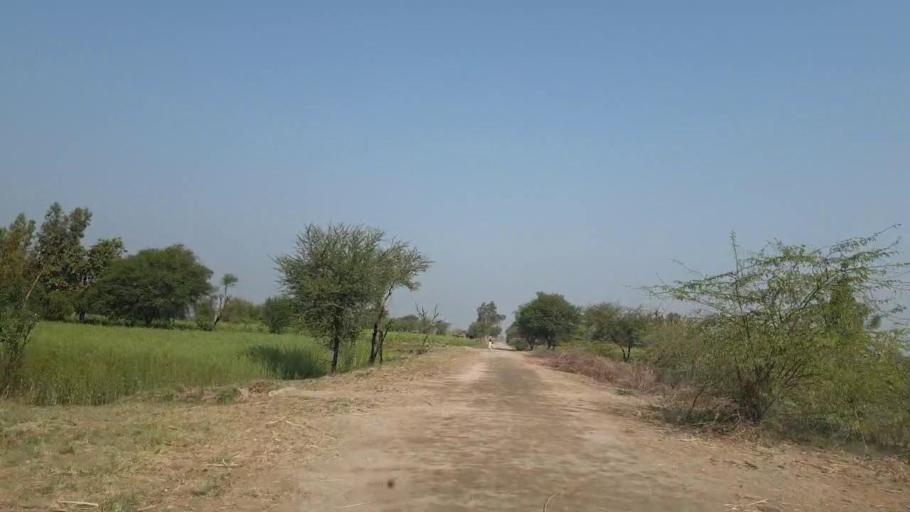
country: PK
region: Sindh
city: Mirpur Khas
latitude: 25.5882
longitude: 69.0150
